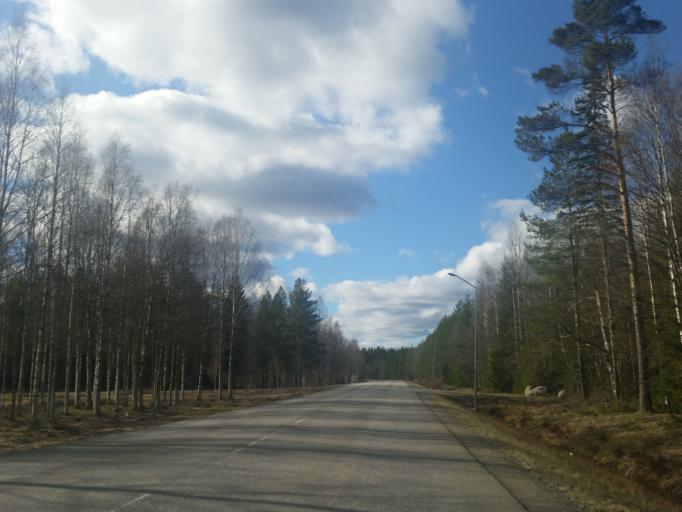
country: SE
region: Vaesterbotten
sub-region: Robertsfors Kommun
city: Robertsfors
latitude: 64.1983
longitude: 20.8357
